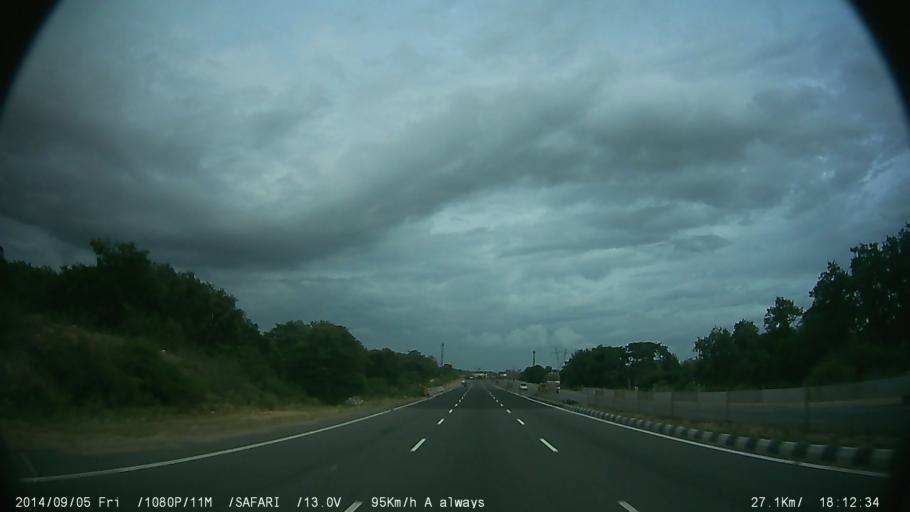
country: IN
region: Tamil Nadu
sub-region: Krishnagiri
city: Hosur
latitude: 12.6919
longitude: 77.9188
